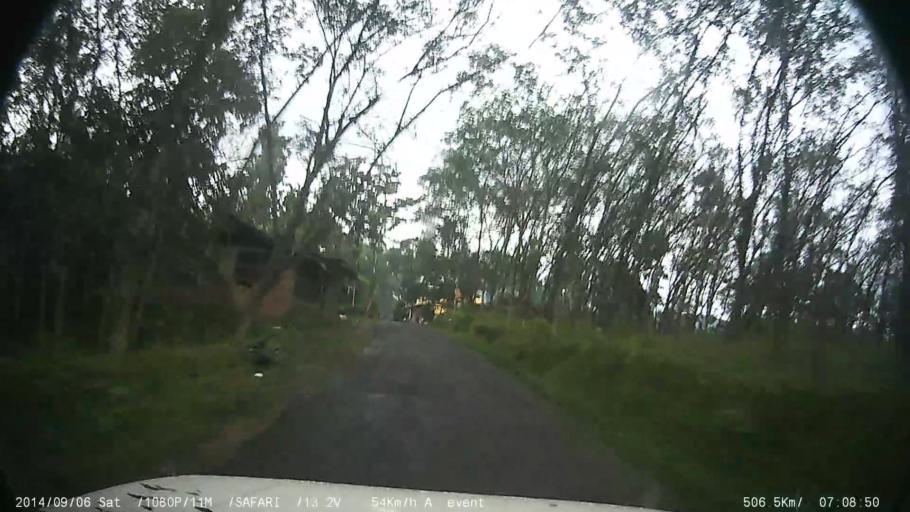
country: IN
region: Kerala
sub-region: Ernakulam
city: Piravam
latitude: 9.7943
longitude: 76.5458
